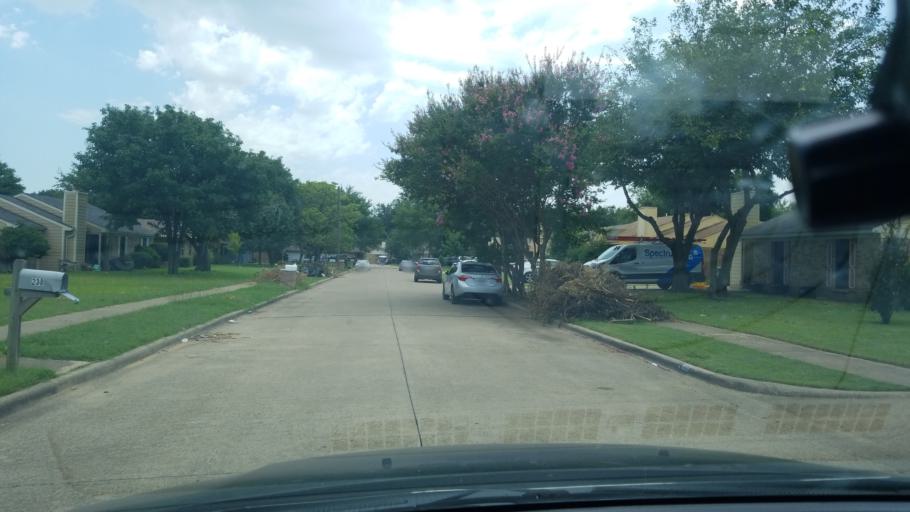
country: US
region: Texas
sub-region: Dallas County
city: Balch Springs
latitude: 32.7148
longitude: -96.6618
